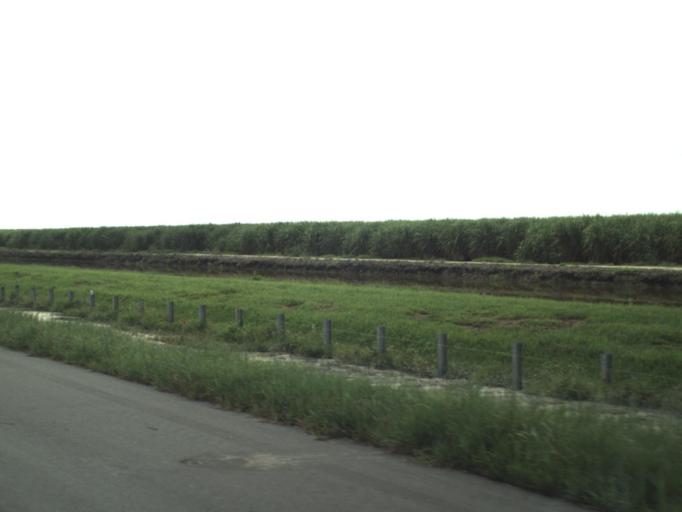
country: US
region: Florida
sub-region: Palm Beach County
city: Belle Glade
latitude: 26.7261
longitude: -80.6182
